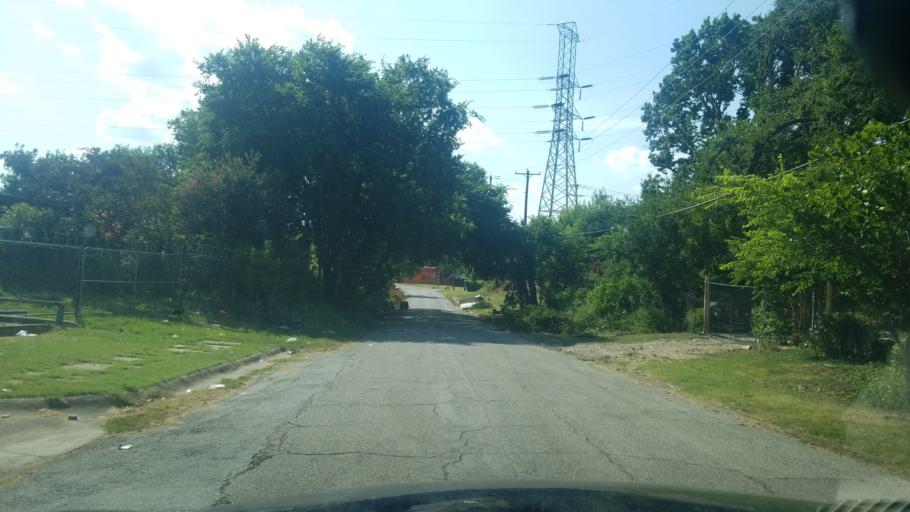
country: US
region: Texas
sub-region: Dallas County
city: Dallas
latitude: 32.7207
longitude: -96.8060
